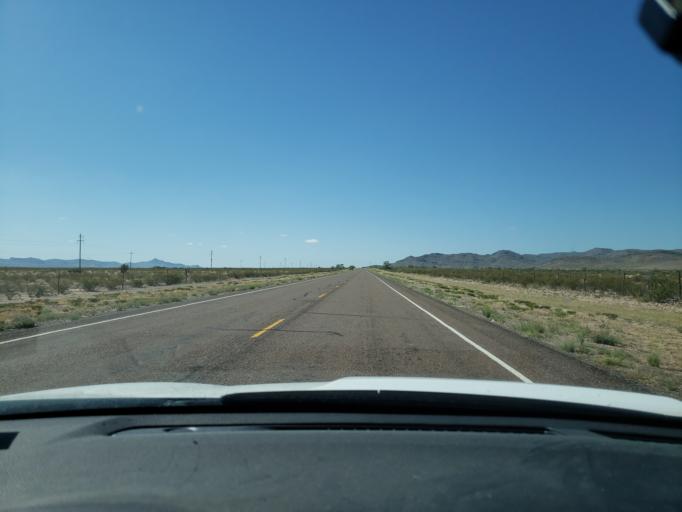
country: US
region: Texas
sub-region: Culberson County
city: Van Horn
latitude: 30.9402
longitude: -104.8111
